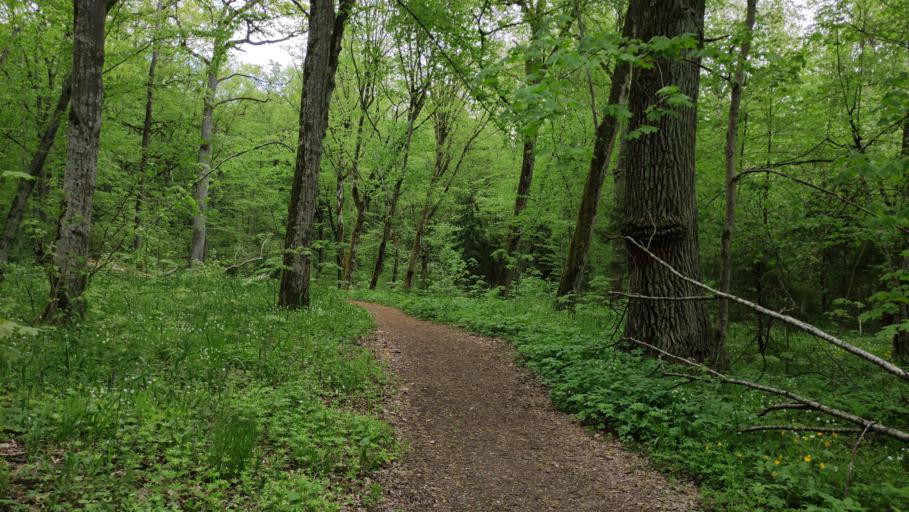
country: LT
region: Alytaus apskritis
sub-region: Alytus
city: Alytus
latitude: 54.3804
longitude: 24.0135
